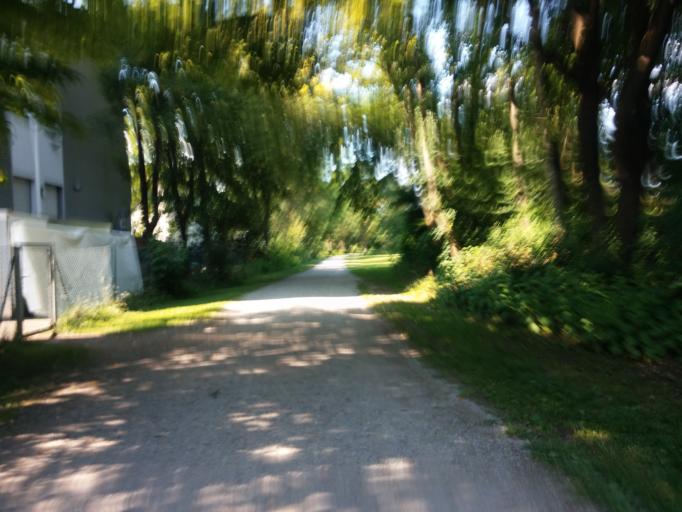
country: DE
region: Bavaria
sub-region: Upper Bavaria
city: Neubiberg
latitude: 48.1329
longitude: 11.6706
